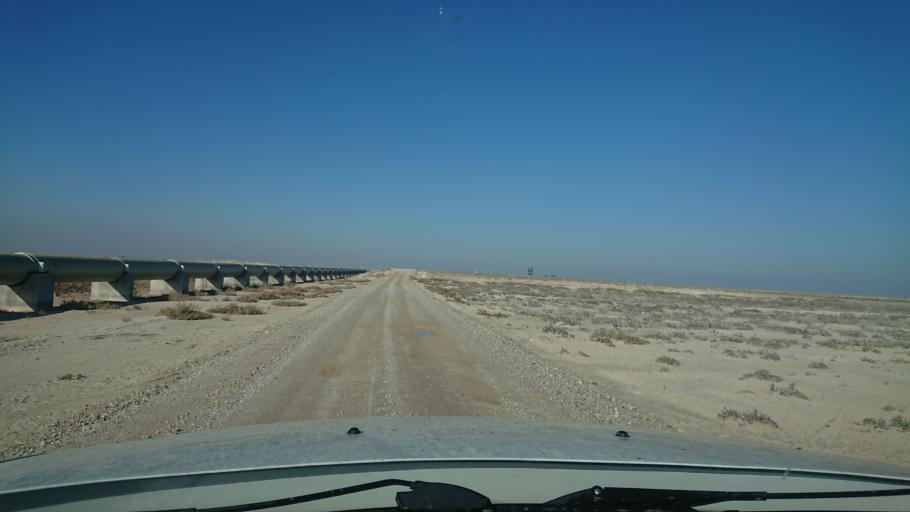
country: TR
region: Aksaray
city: Eskil
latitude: 38.4193
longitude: 33.5027
